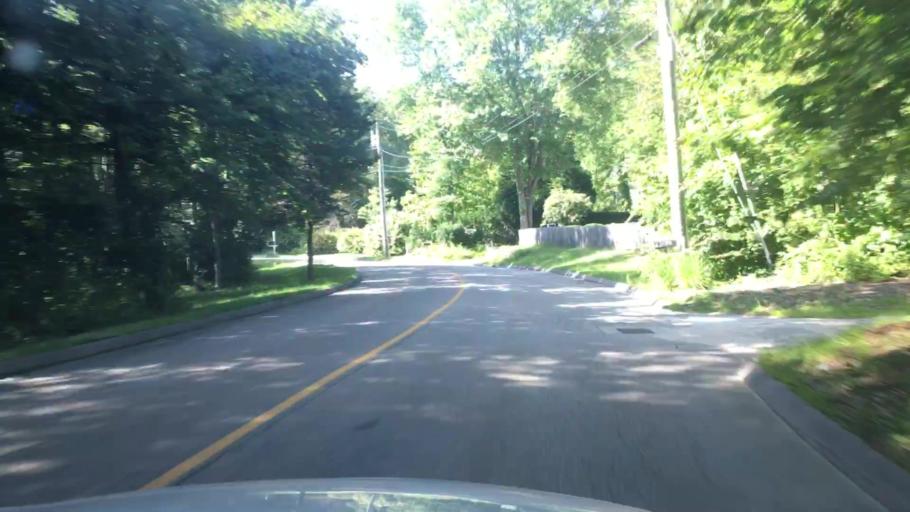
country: US
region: Connecticut
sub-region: Middlesex County
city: Deep River Center
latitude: 41.3675
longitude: -72.4439
